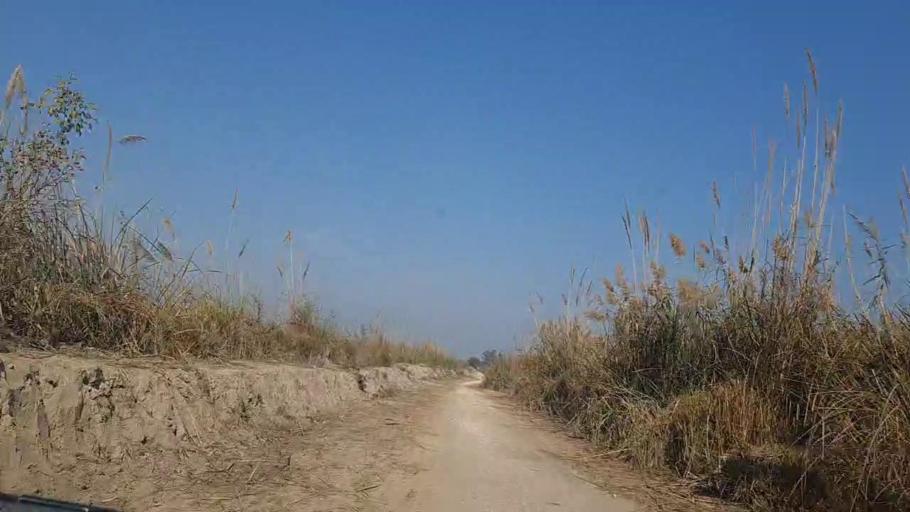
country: PK
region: Sindh
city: Sakrand
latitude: 26.0873
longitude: 68.3662
